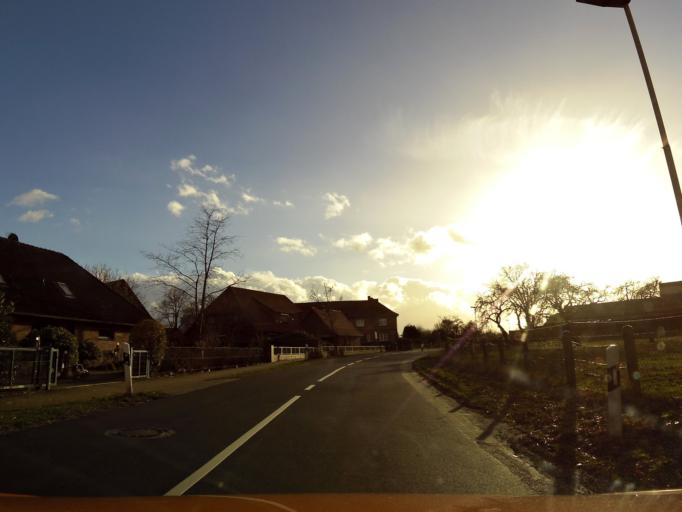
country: DE
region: Lower Saxony
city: Langwedel
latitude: 52.9578
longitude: 9.1931
